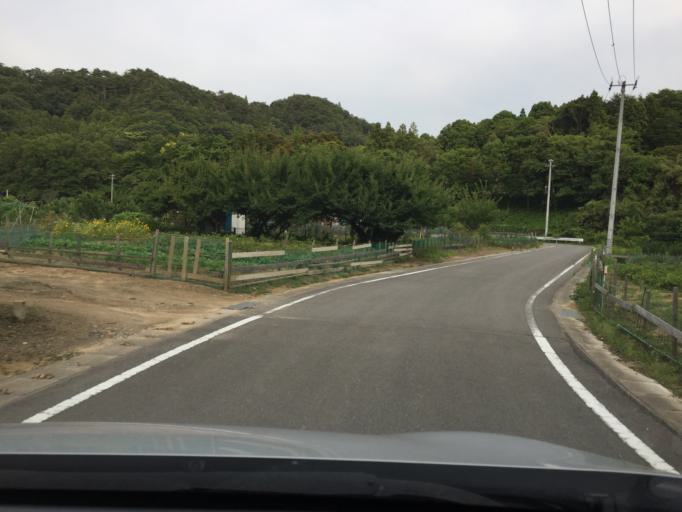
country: JP
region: Fukushima
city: Iwaki
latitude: 37.0443
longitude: 140.9182
